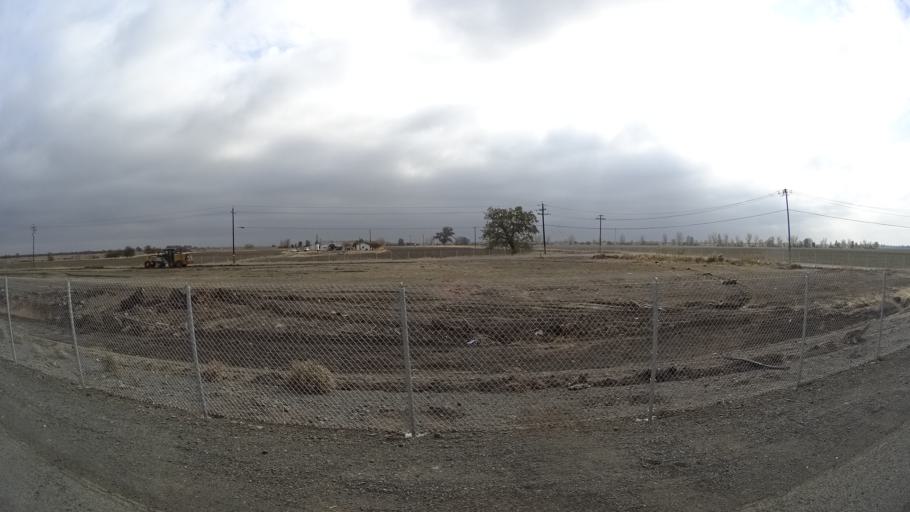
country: US
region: California
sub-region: Yolo County
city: Esparto
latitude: 38.7099
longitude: -122.0126
